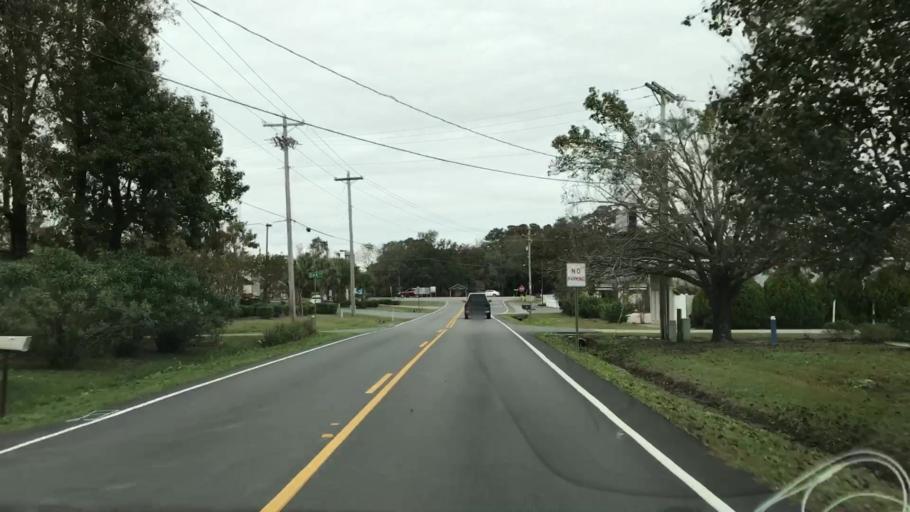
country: US
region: South Carolina
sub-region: Horry County
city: Garden City
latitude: 33.5893
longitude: -79.0050
